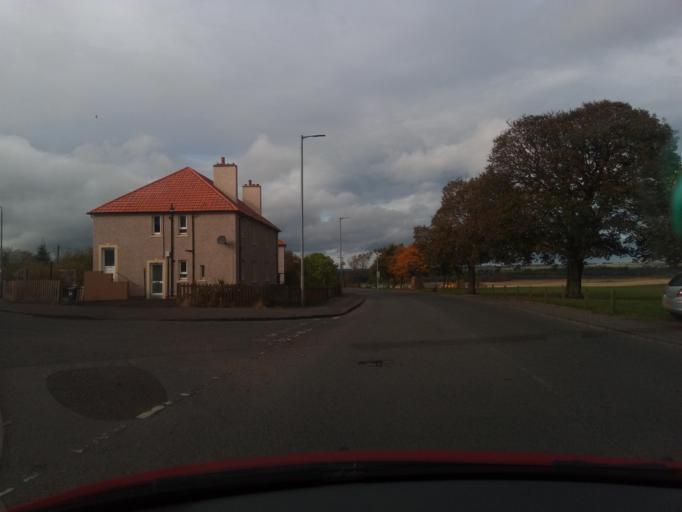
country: GB
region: Scotland
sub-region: South Lanarkshire
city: Carnwath
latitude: 55.7010
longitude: -3.6167
